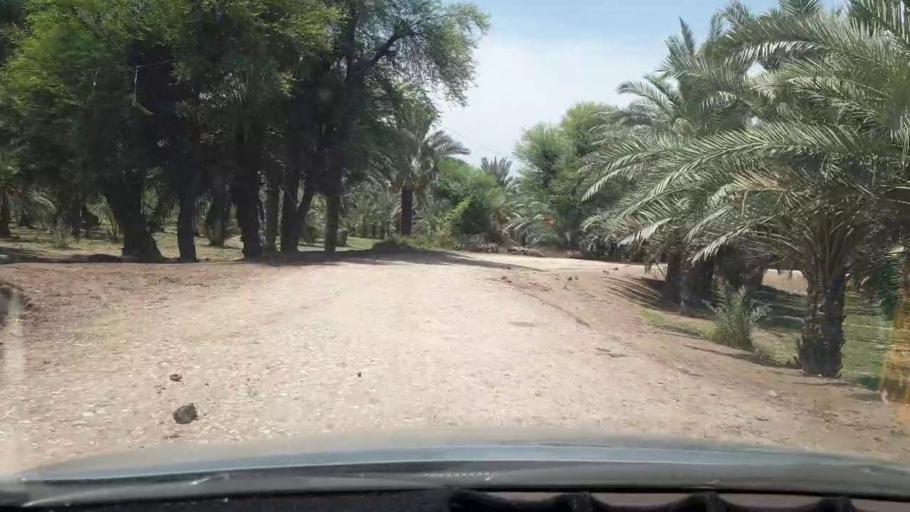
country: PK
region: Sindh
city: Khairpur
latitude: 27.4753
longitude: 68.7607
